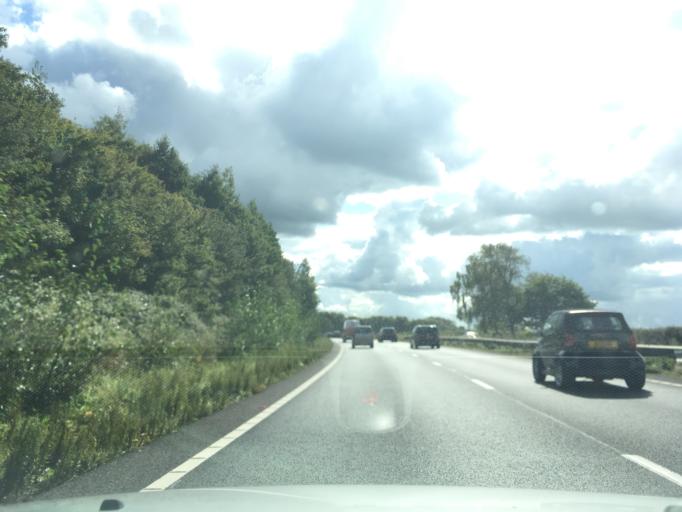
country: GB
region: England
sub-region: Surrey
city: Milford
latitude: 51.2047
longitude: -0.6504
